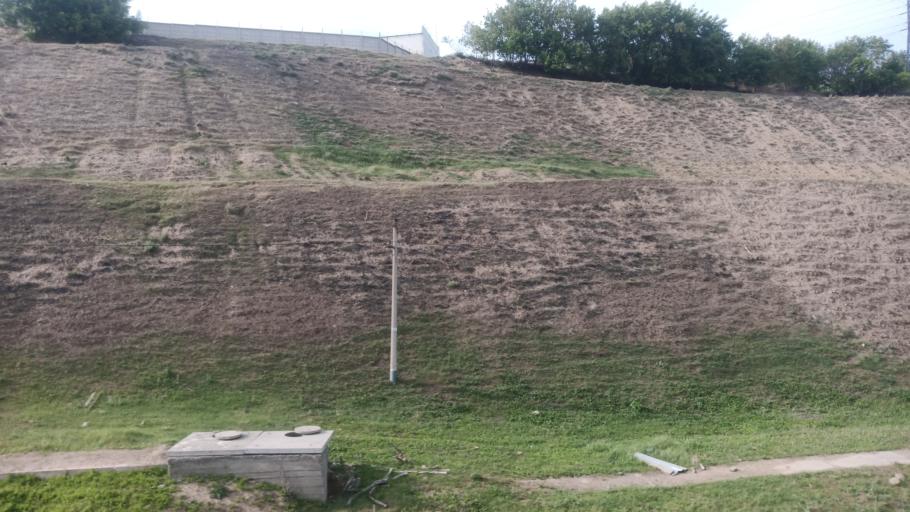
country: RU
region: Altai Krai
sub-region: Gorod Barnaulskiy
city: Barnaul
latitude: 53.3740
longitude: 83.8025
